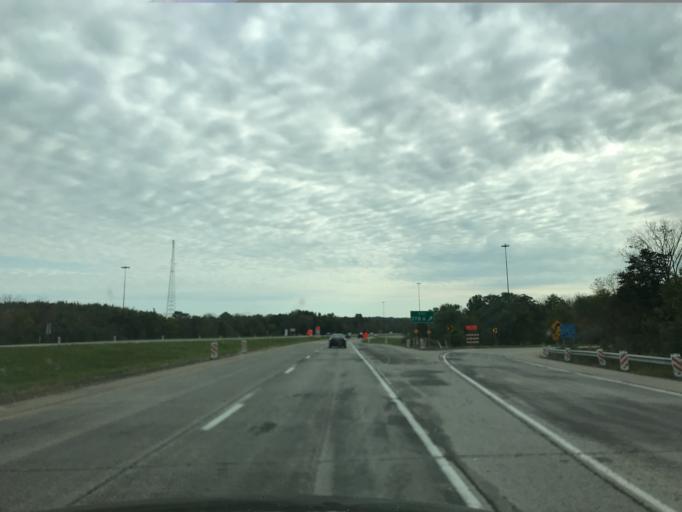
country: US
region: Pennsylvania
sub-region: Erie County
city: Erie
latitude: 42.0308
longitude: -80.1227
